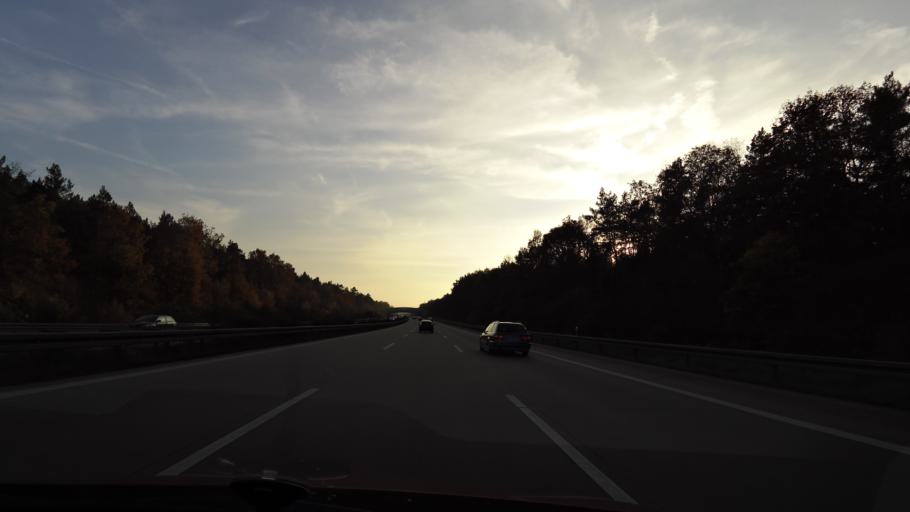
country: DE
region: Brandenburg
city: Niemegk
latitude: 52.0720
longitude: 12.6597
